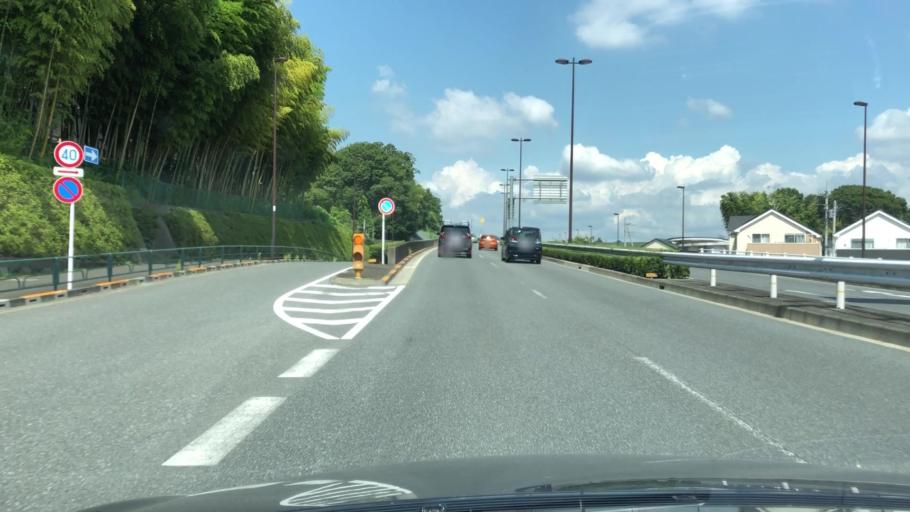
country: JP
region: Tokyo
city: Hachioji
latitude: 35.6904
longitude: 139.3318
